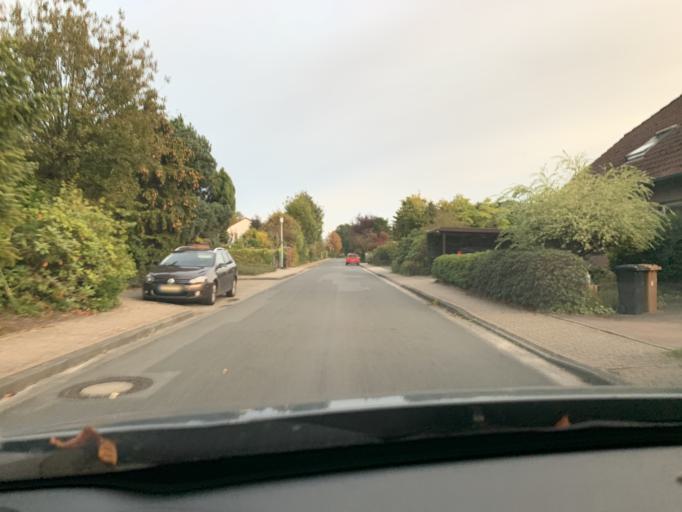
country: DE
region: Lower Saxony
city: Westerstede
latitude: 53.2558
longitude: 7.9047
